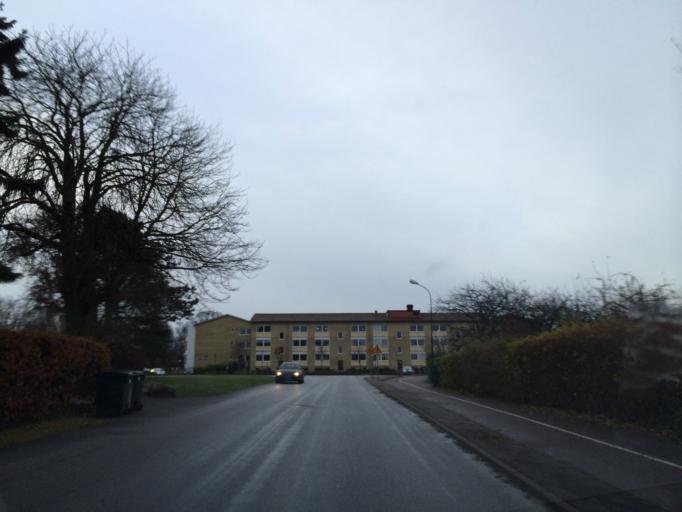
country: SE
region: Skane
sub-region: Lomma Kommun
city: Lomma
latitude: 55.6756
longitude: 13.0862
